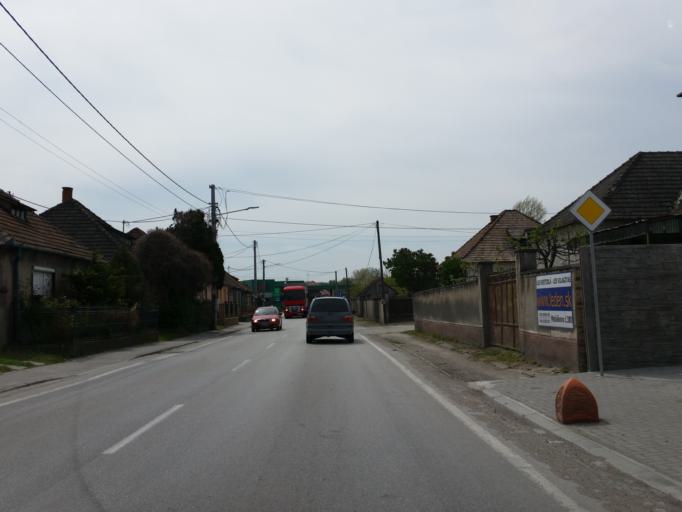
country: SK
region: Nitriansky
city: Sellye
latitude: 48.0146
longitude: 17.8007
